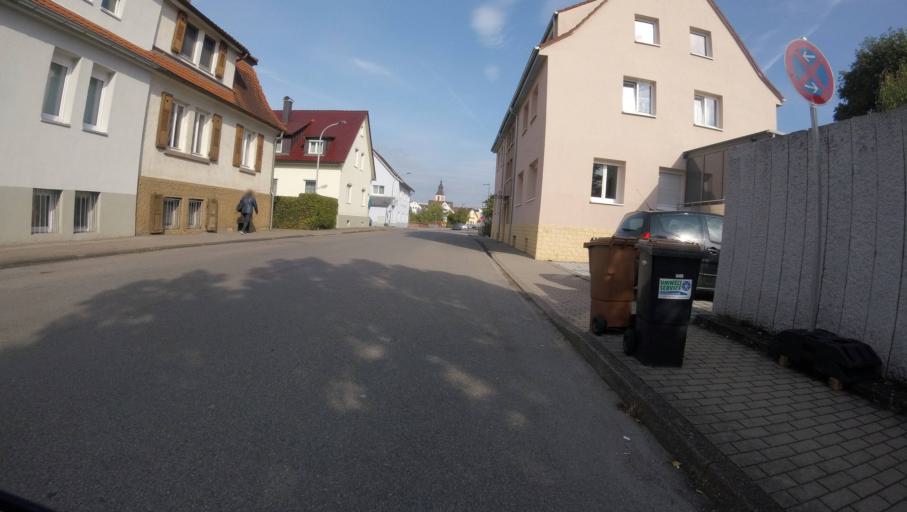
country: DE
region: Baden-Wuerttemberg
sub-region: Karlsruhe Region
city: Nagold
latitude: 48.5472
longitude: 8.7252
